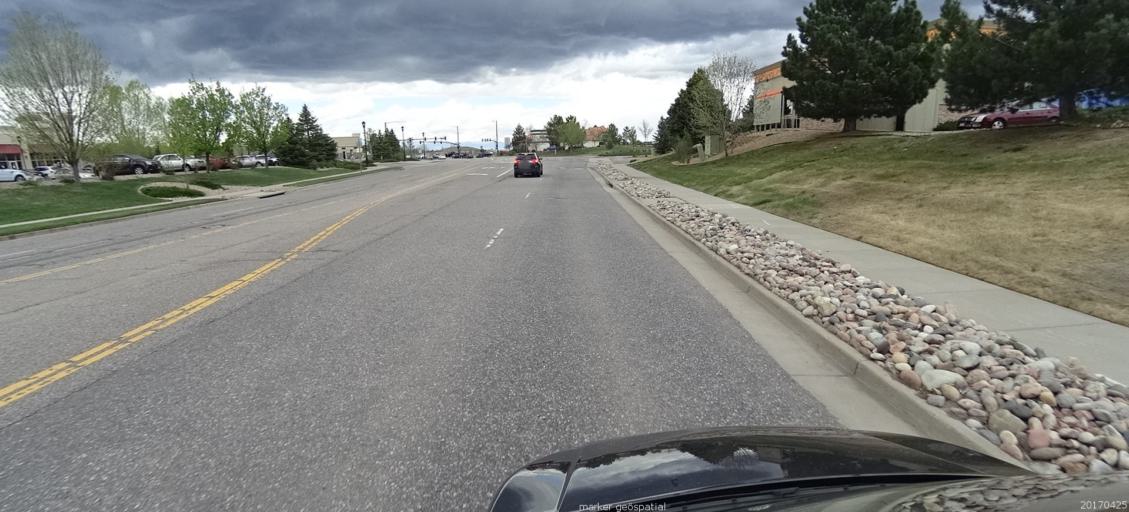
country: US
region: Colorado
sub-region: Adams County
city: Lone Tree
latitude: 39.5545
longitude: -104.8815
